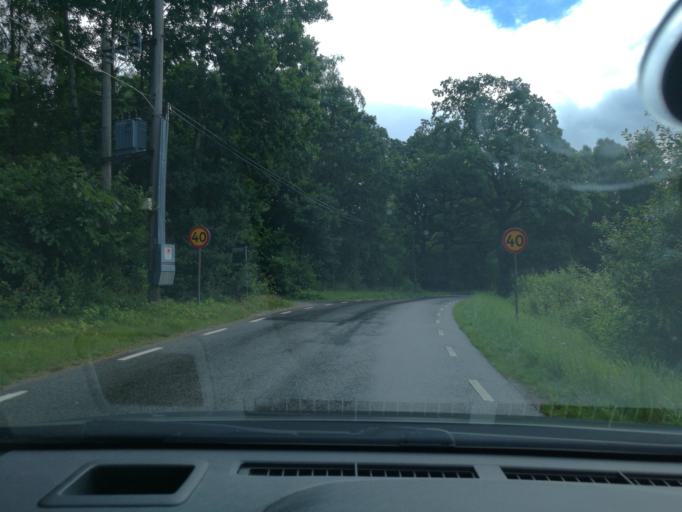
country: SE
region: Skane
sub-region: Hoors Kommun
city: Hoeoer
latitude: 55.9152
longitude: 13.4779
